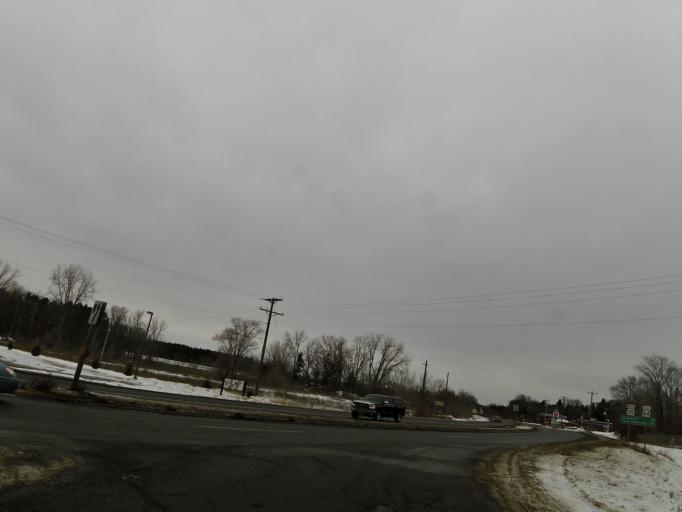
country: US
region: Minnesota
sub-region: Washington County
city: Stillwater
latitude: 45.0646
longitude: -92.7919
